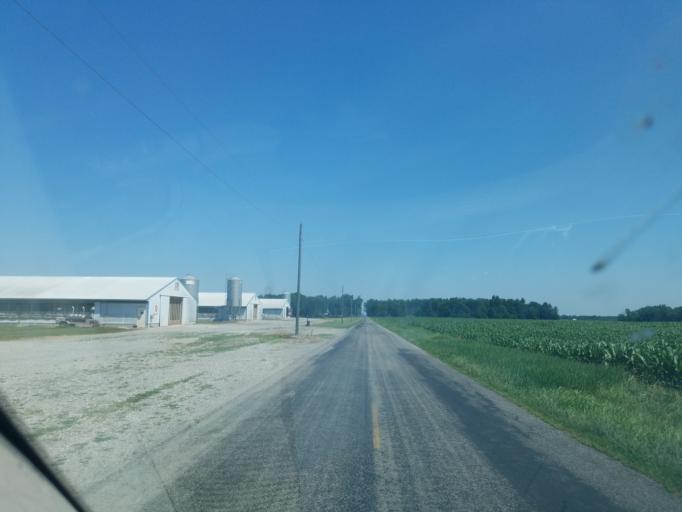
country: US
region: Ohio
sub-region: Mercer County
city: Saint Henry
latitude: 40.4519
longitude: -84.7080
